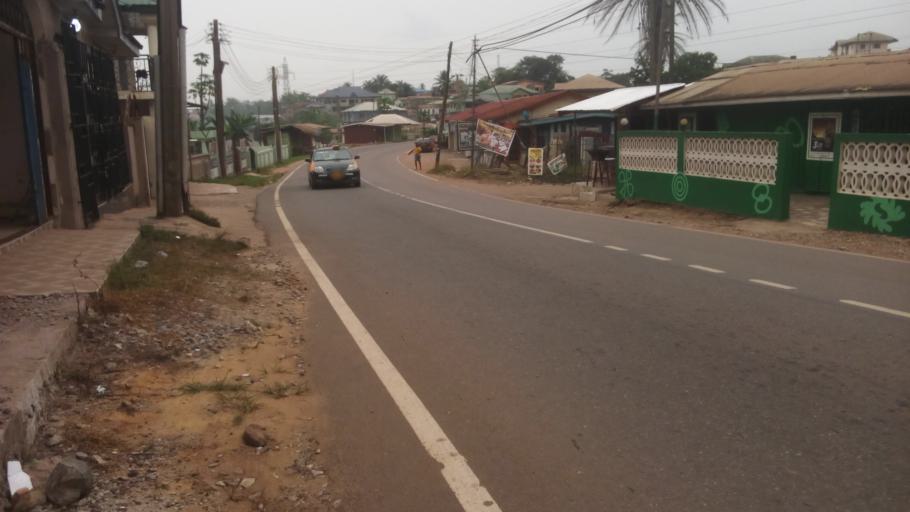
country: GH
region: Western
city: Tarkwa
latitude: 5.2859
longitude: -2.0005
